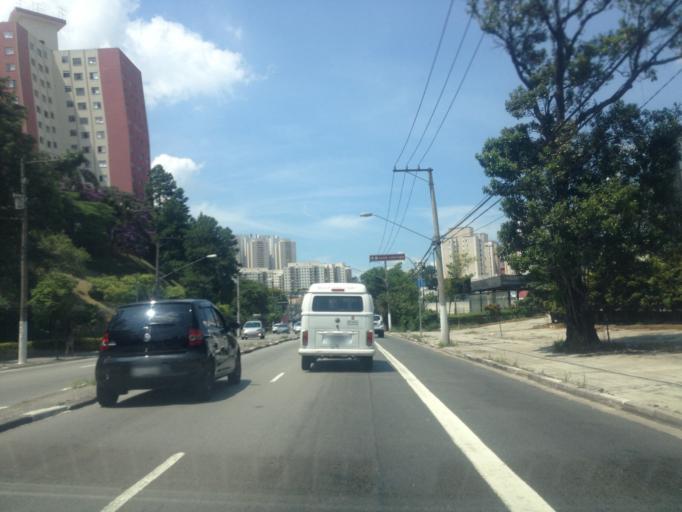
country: BR
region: Sao Paulo
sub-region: Diadema
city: Diadema
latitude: -23.6619
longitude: -46.6793
